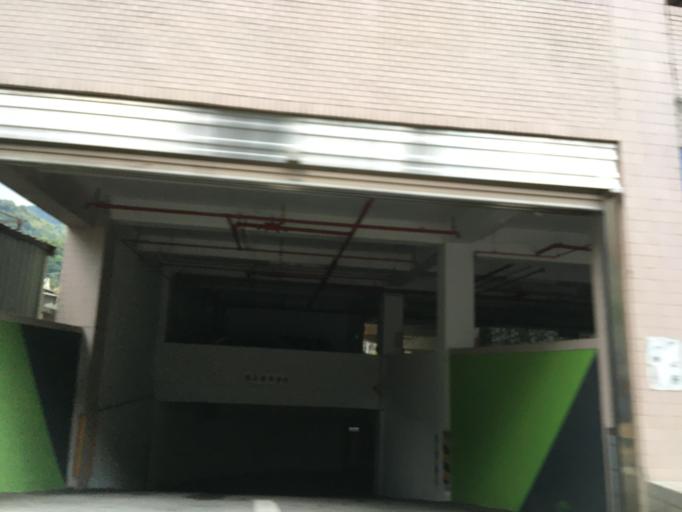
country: TW
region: Taiwan
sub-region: Yilan
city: Yilan
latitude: 24.9357
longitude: 121.7103
